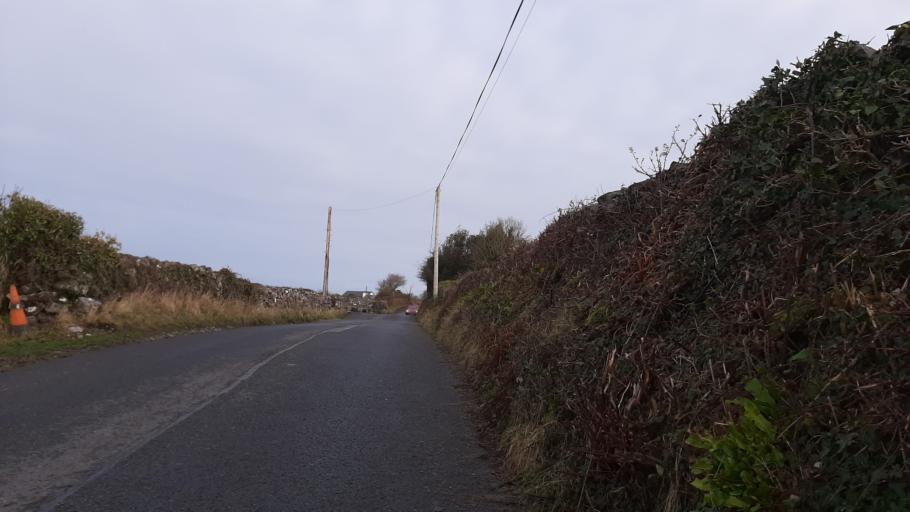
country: IE
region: Connaught
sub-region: County Galway
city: Gaillimh
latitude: 53.3116
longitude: -9.0544
